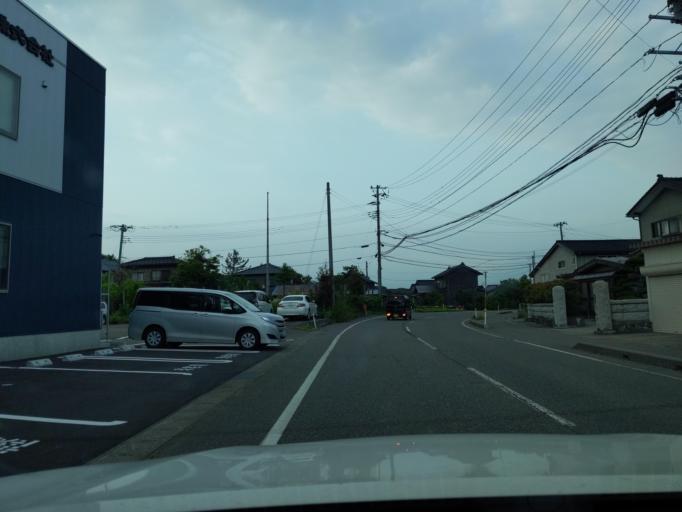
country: JP
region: Niigata
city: Kashiwazaki
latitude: 37.4163
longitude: 138.6125
